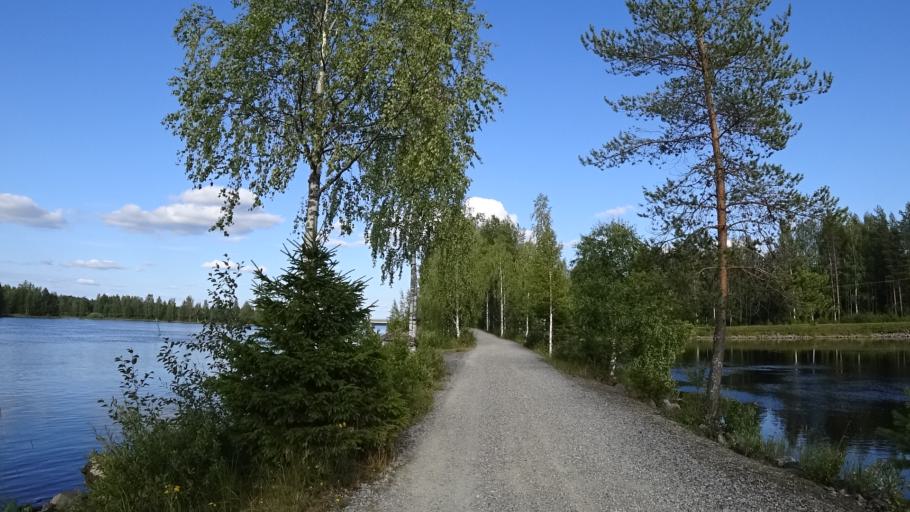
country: FI
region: North Karelia
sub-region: Joensuu
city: Eno
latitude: 62.8012
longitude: 30.1459
